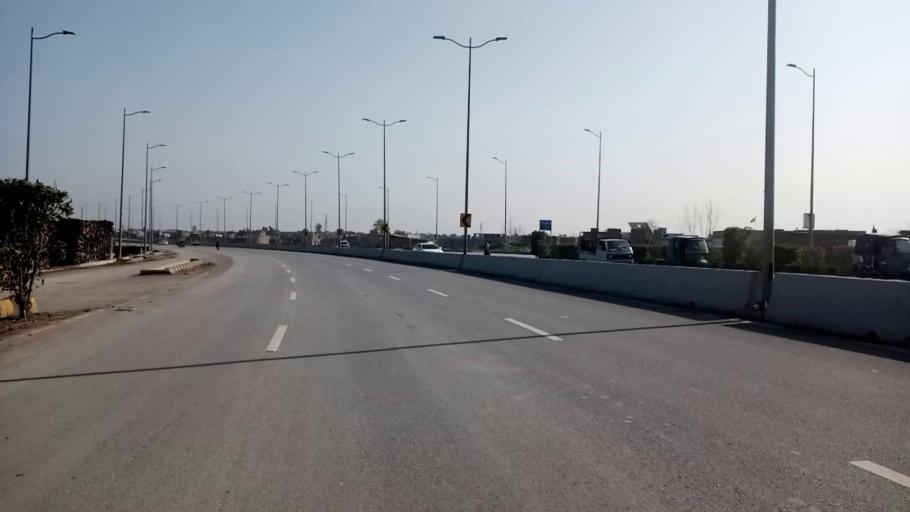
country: PK
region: Khyber Pakhtunkhwa
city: Peshawar
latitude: 34.0318
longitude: 71.5433
